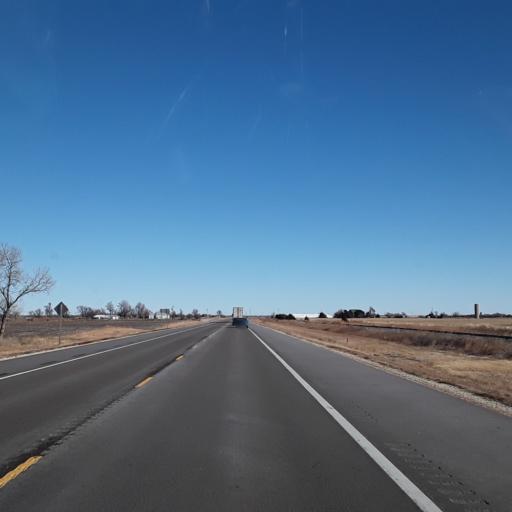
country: US
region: Kansas
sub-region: Pawnee County
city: Larned
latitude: 38.1954
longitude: -99.0758
